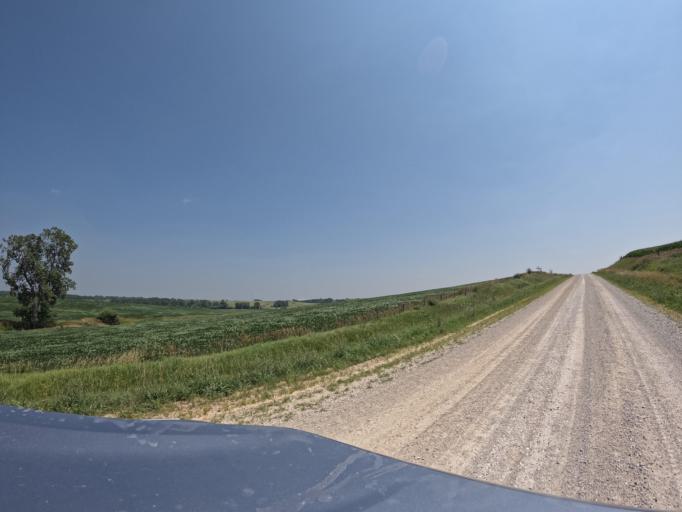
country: US
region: Iowa
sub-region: Keokuk County
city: Sigourney
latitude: 41.3305
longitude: -92.2385
